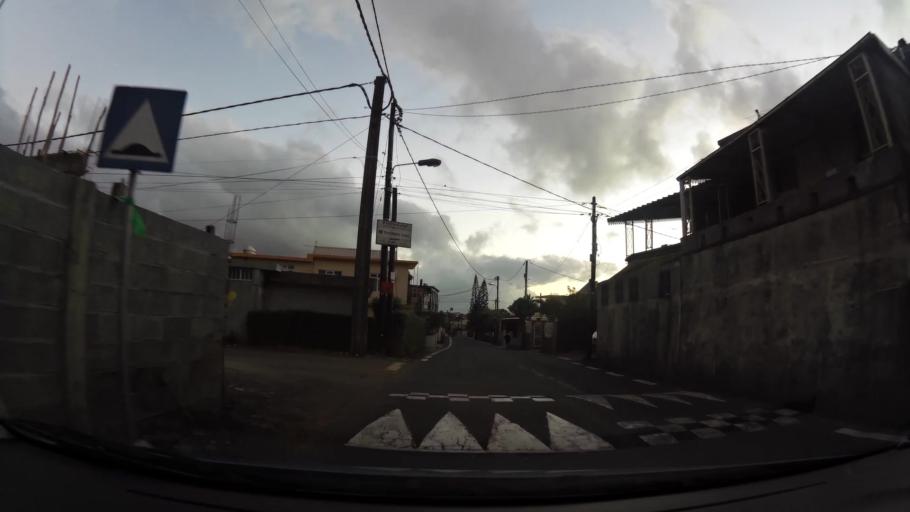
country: MU
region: Plaines Wilhems
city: Curepipe
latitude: -20.2908
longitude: 57.5226
